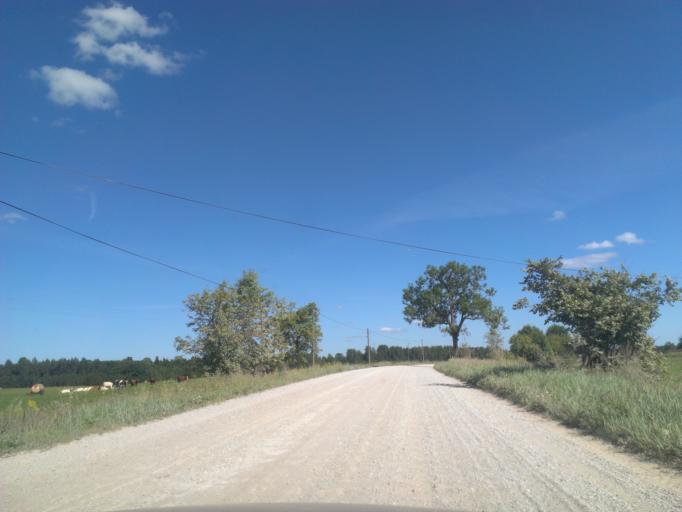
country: LV
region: Malpils
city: Malpils
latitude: 57.0158
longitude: 24.9955
